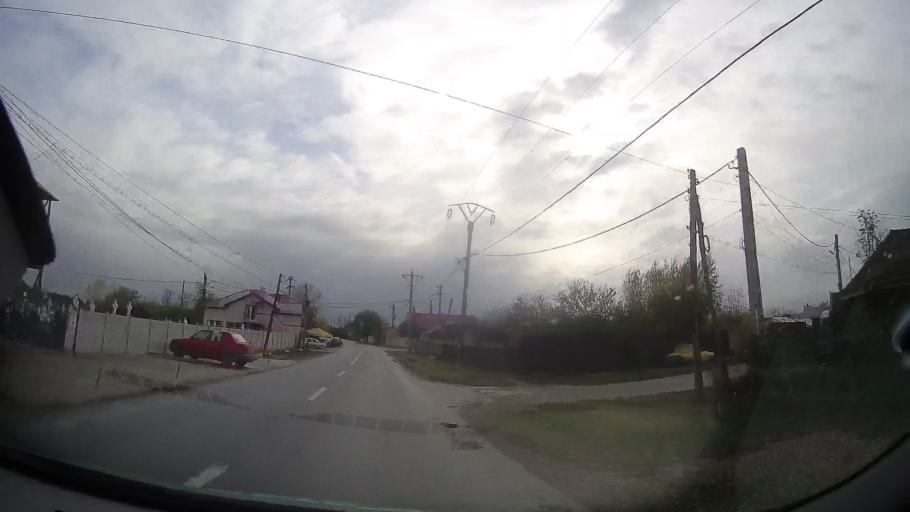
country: RO
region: Ialomita
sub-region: Comuna Fierbinti-Targ
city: Fierbintii de Jos
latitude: 44.6966
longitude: 26.3942
